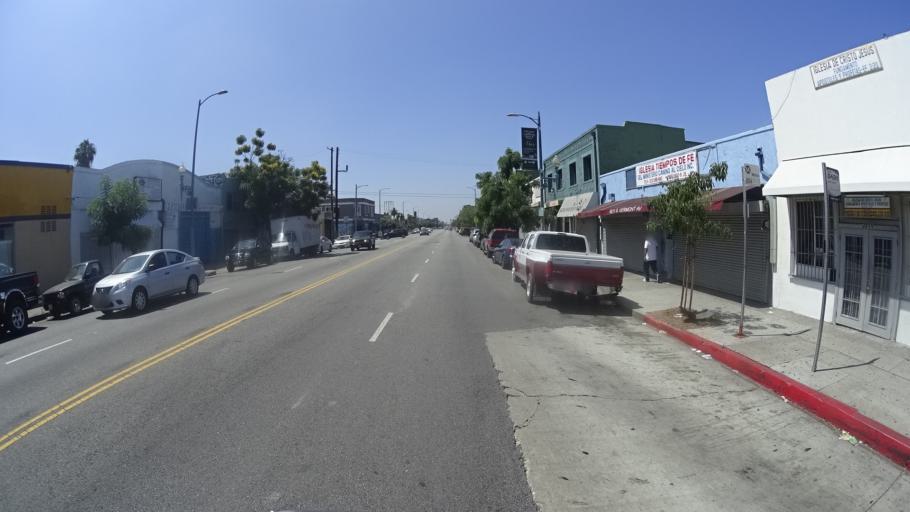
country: US
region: California
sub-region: Los Angeles County
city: View Park-Windsor Hills
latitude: 33.9995
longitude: -118.2916
